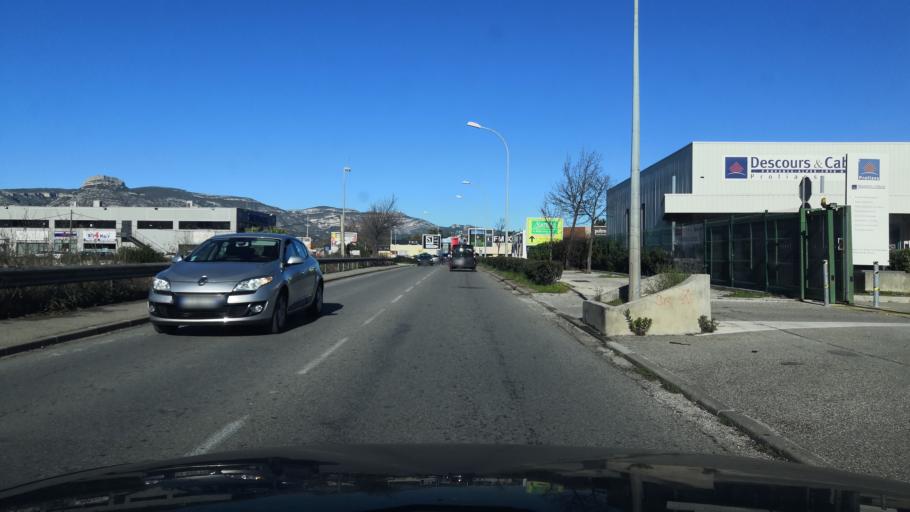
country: FR
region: Provence-Alpes-Cote d'Azur
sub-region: Departement des Bouches-du-Rhone
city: Aubagne
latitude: 43.2875
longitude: 5.5944
